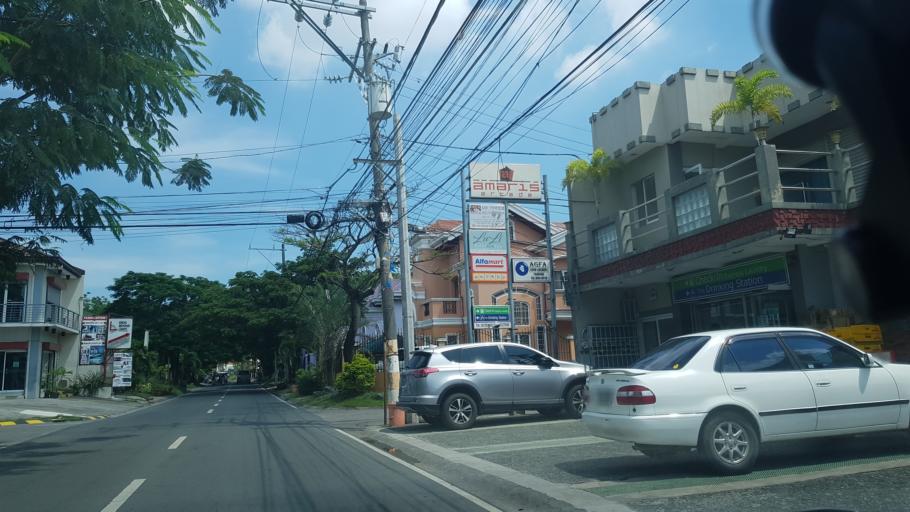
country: PH
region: Calabarzon
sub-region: Province of Rizal
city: Las Pinas
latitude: 14.4317
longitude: 120.9943
